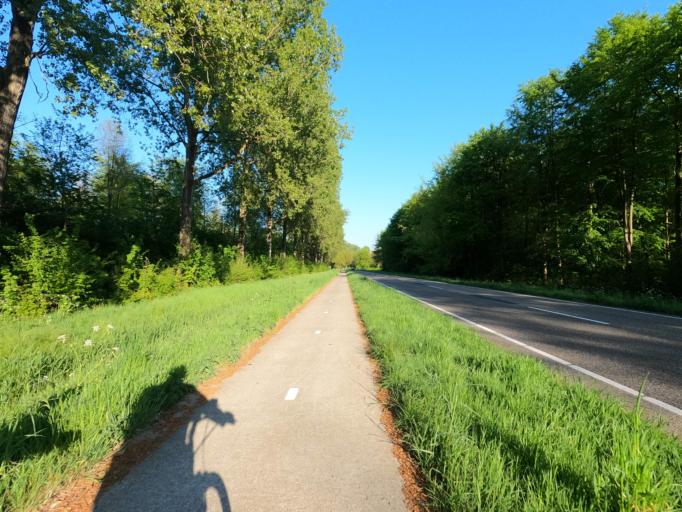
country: NL
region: Flevoland
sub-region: Gemeente Zeewolde
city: Zeewolde
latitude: 52.3083
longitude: 5.5248
